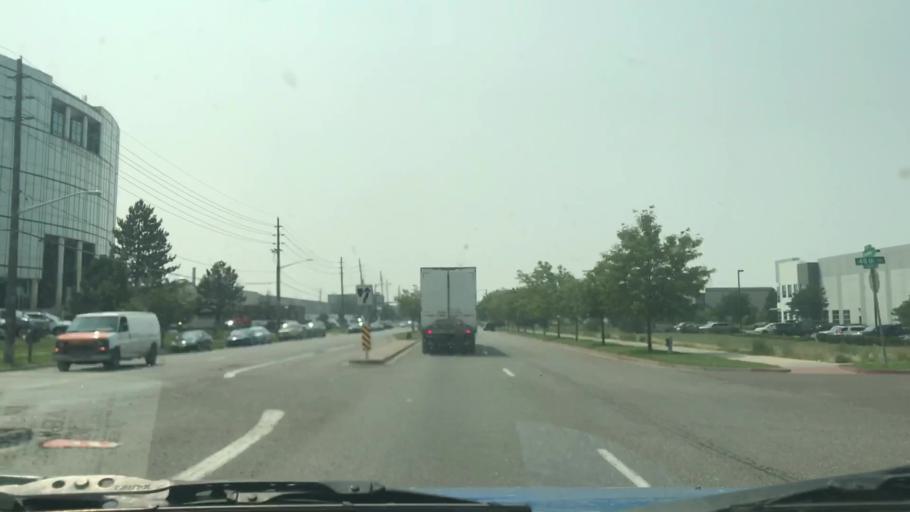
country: US
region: Colorado
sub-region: Adams County
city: Aurora
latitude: 39.7850
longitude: -104.8659
